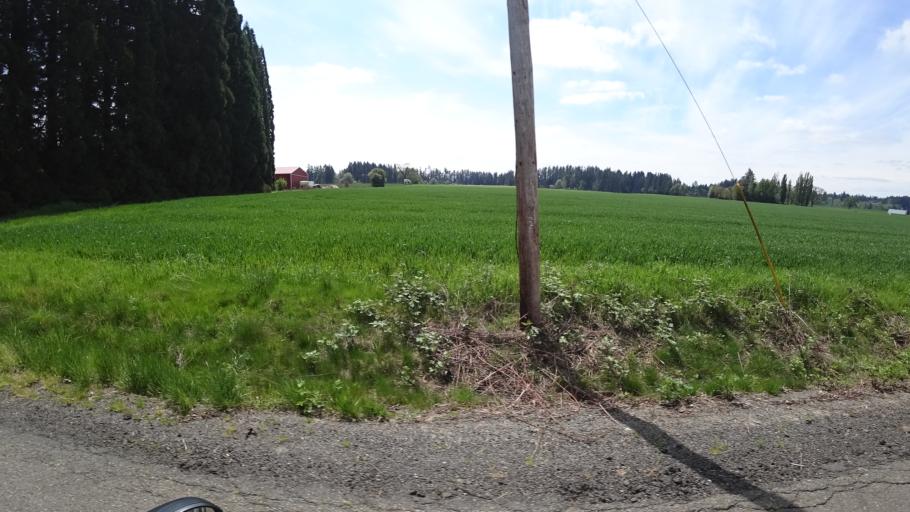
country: US
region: Oregon
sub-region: Washington County
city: North Plains
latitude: 45.5721
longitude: -122.9657
